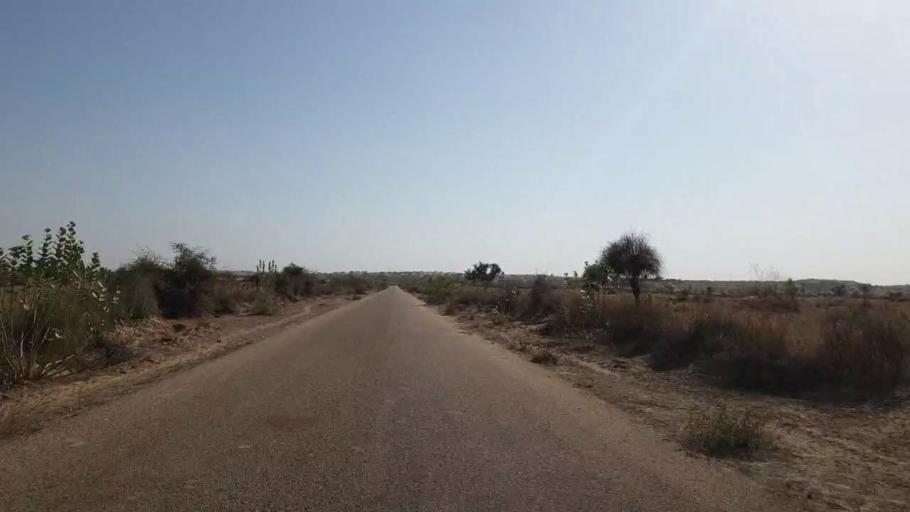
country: PK
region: Sindh
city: Islamkot
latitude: 25.0706
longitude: 70.0422
